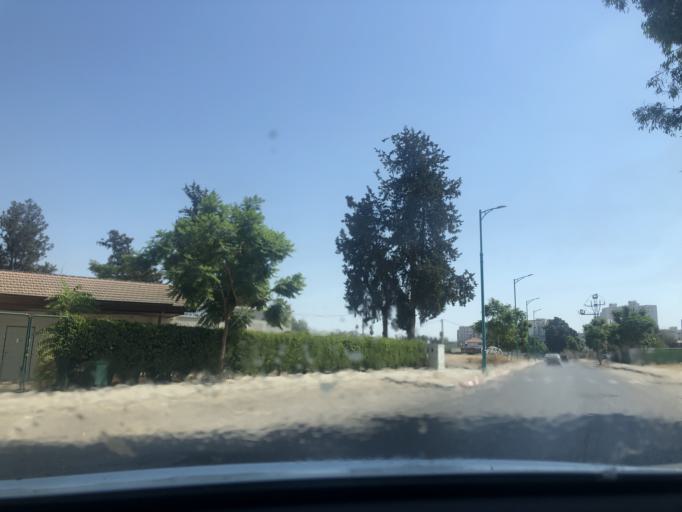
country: IL
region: Central District
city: Lod
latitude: 31.9593
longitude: 34.8972
